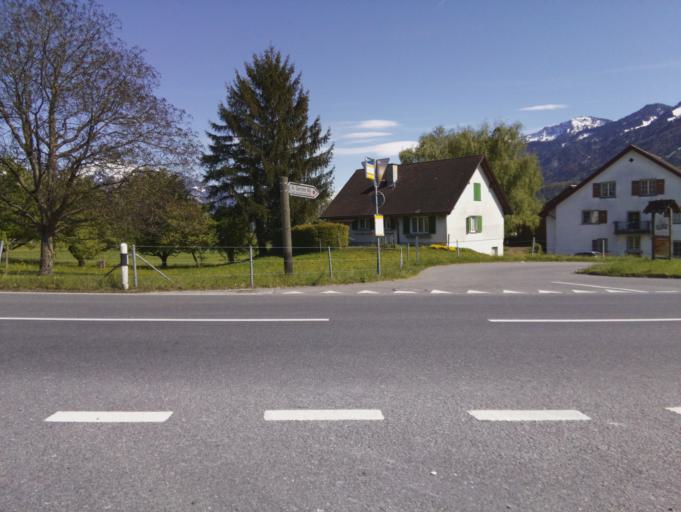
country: CH
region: Schwyz
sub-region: Bezirk March
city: Tuggen
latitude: 47.1850
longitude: 8.9433
